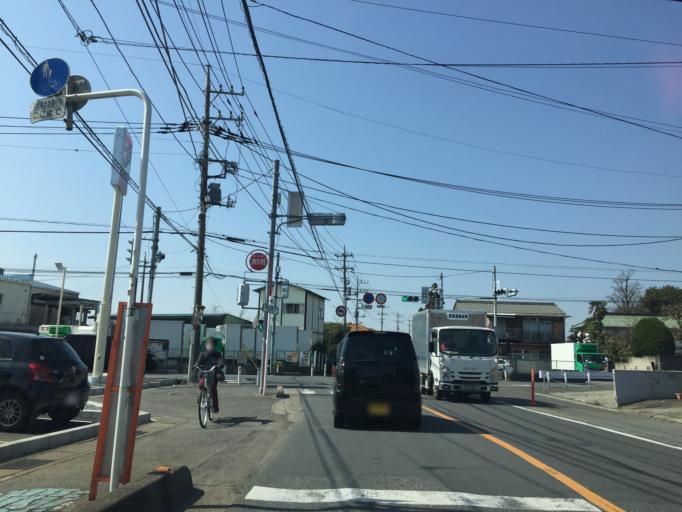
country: JP
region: Saitama
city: Shiki
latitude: 35.8501
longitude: 139.5864
